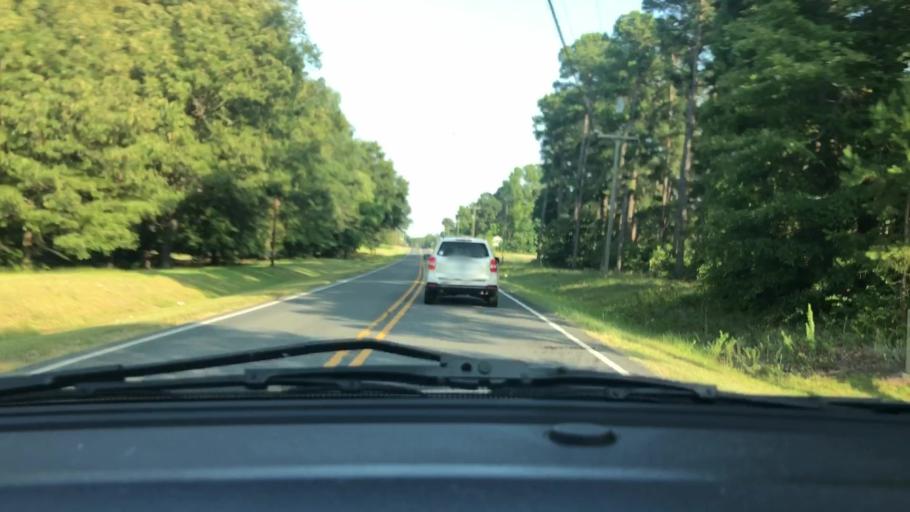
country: US
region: North Carolina
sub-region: Lee County
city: Broadway
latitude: 35.3537
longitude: -79.0761
